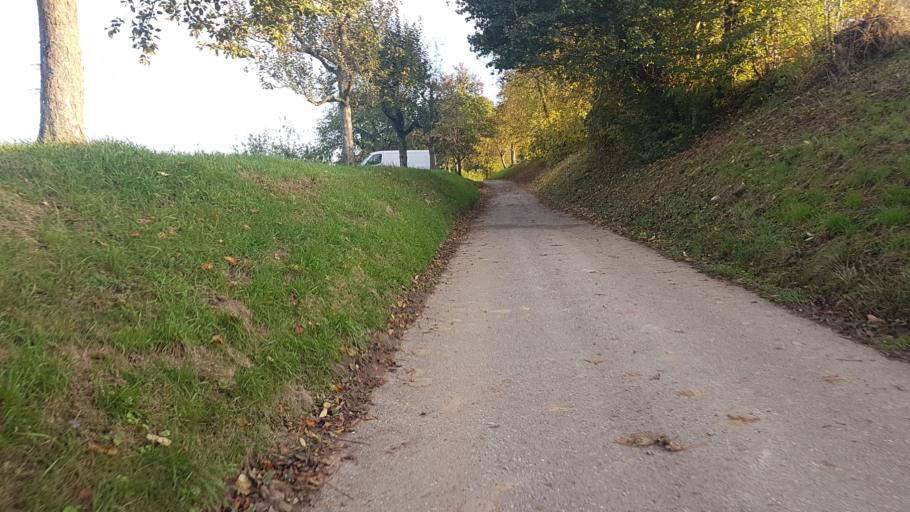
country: DE
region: Baden-Wuerttemberg
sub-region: Karlsruhe Region
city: Neckarzimmern
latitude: 49.3197
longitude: 9.1133
